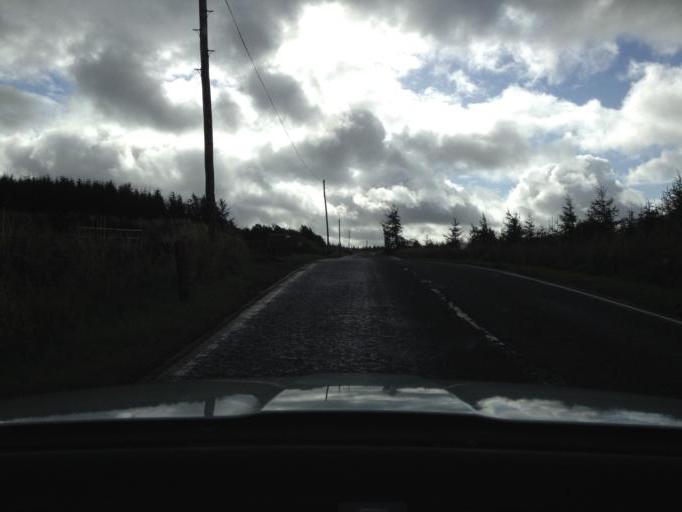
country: GB
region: Scotland
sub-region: West Lothian
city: West Calder
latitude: 55.8199
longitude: -3.5238
